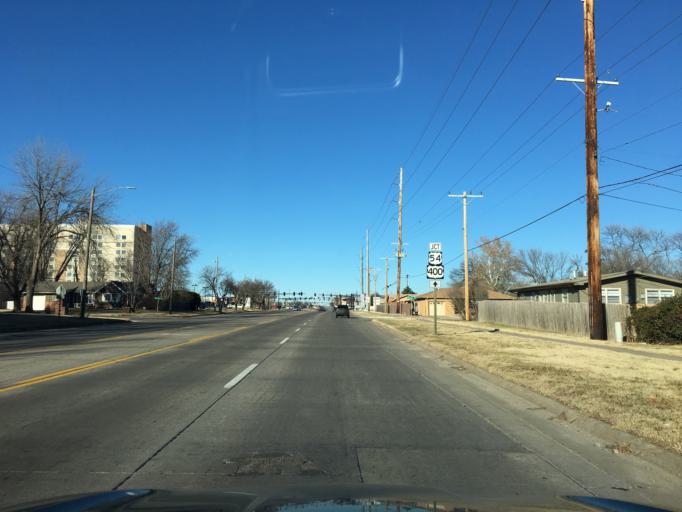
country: US
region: Kansas
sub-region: Sedgwick County
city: Bellaire
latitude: 37.6756
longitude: -97.2444
